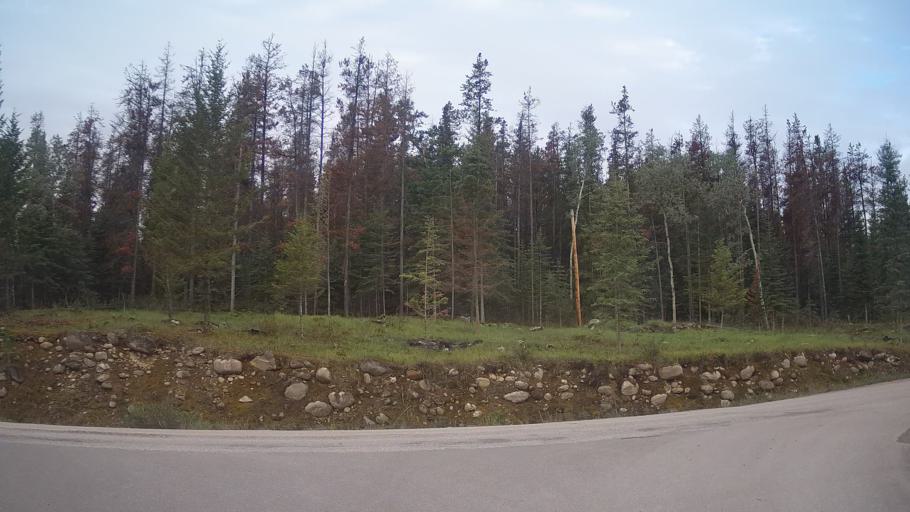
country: CA
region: Alberta
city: Jasper Park Lodge
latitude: 52.8668
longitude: -118.0710
